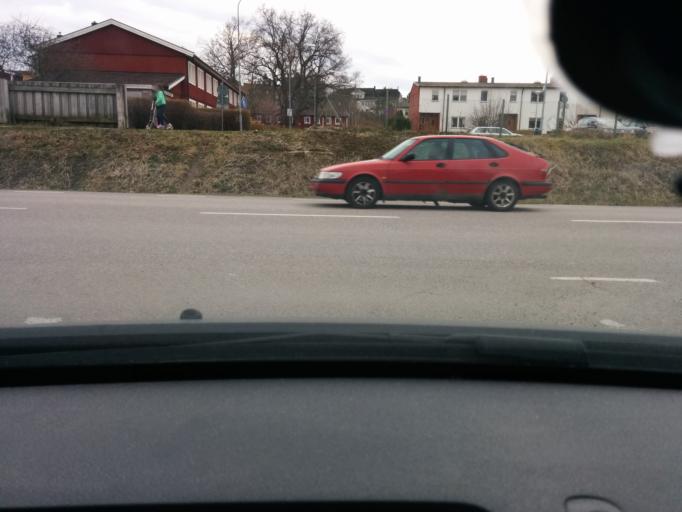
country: SE
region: Stockholm
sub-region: Jarfalla Kommun
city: Jakobsberg
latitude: 59.3807
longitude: 17.8077
